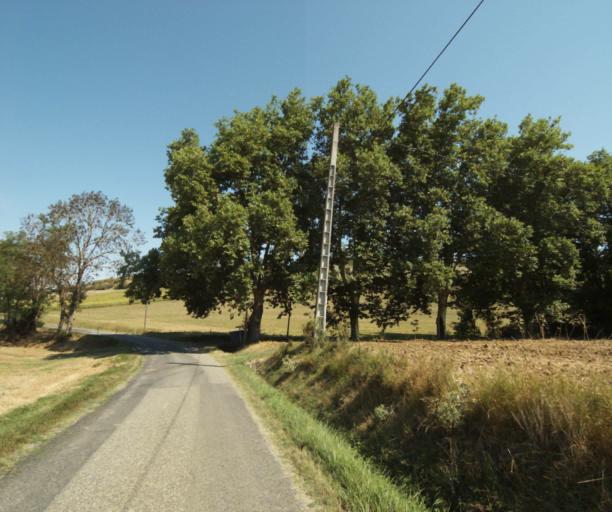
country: FR
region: Midi-Pyrenees
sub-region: Departement de l'Ariege
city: Lezat-sur-Leze
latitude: 43.2680
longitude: 1.3616
